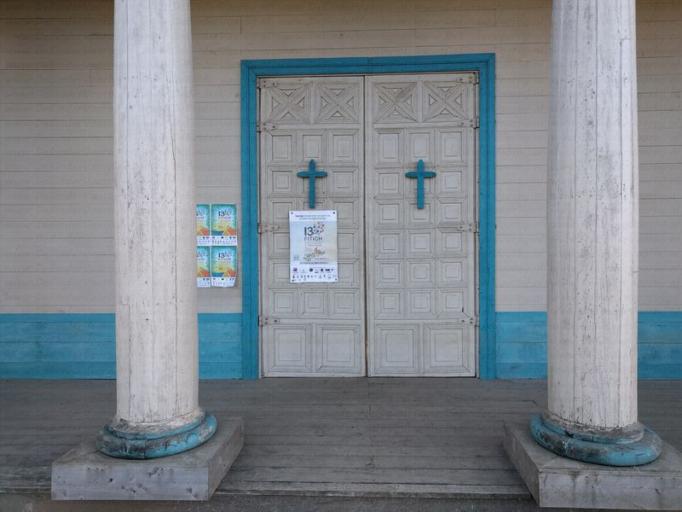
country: CL
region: Los Lagos
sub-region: Provincia de Chiloe
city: Castro
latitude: -42.5014
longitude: -73.7854
